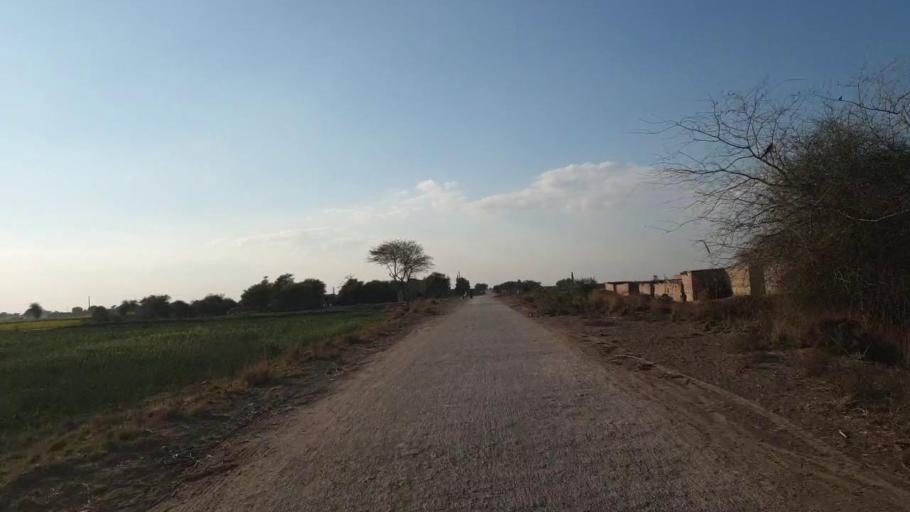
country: PK
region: Sindh
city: Shahpur Chakar
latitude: 26.1436
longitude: 68.5417
